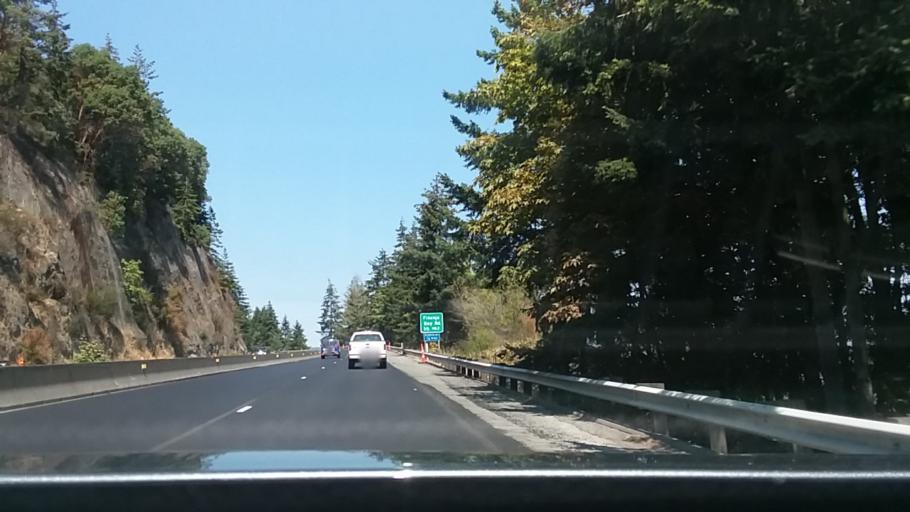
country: US
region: Washington
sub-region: Skagit County
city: Anacortes
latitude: 48.4794
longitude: -122.5929
